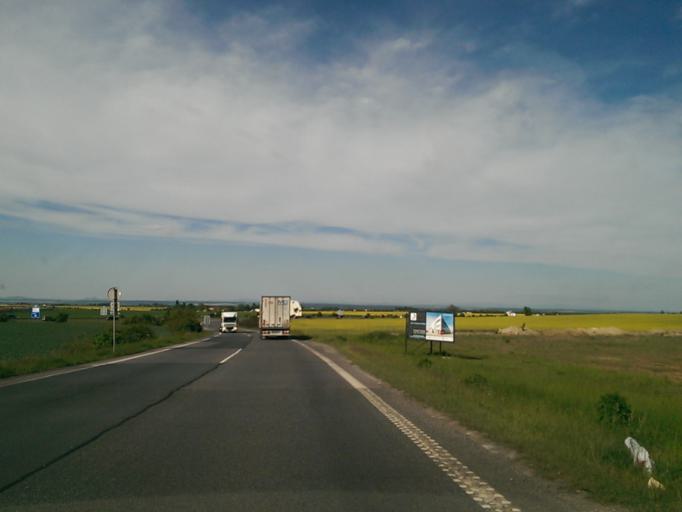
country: CZ
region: Praha
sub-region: Praha 20
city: Horni Pocernice
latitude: 50.1260
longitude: 14.6239
